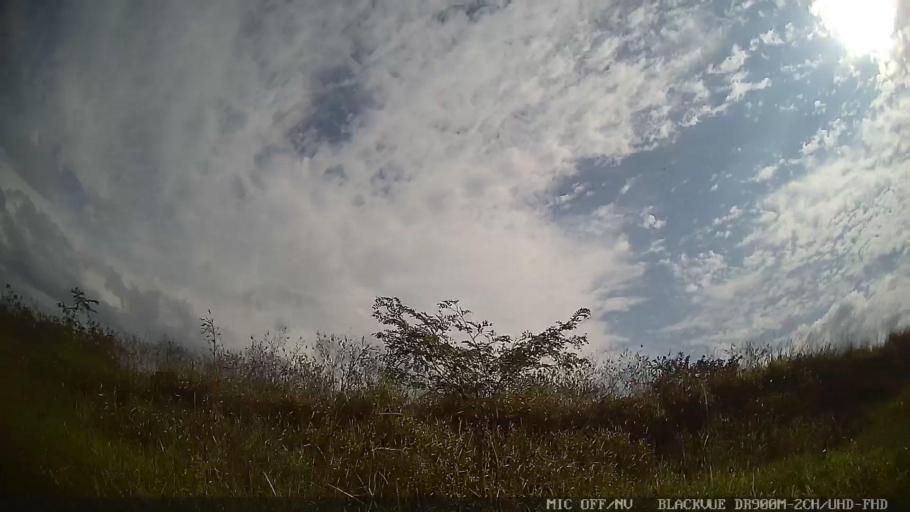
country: BR
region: Sao Paulo
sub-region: Salto
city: Salto
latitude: -23.1749
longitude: -47.2718
